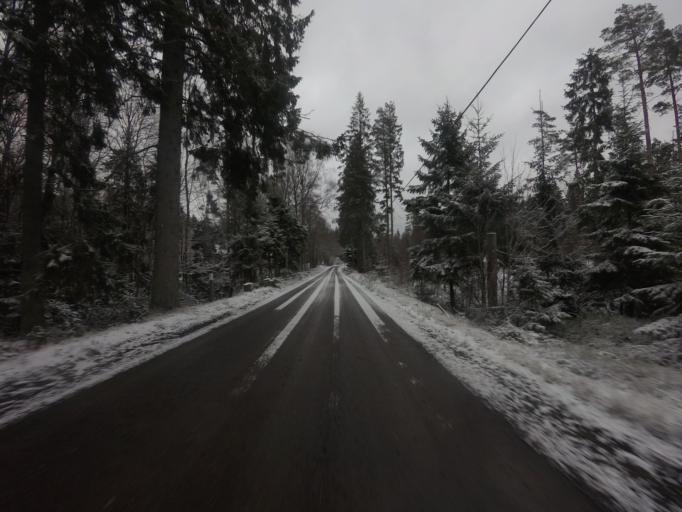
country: SE
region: Skane
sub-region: Osby Kommun
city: Lonsboda
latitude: 56.3918
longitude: 14.2725
